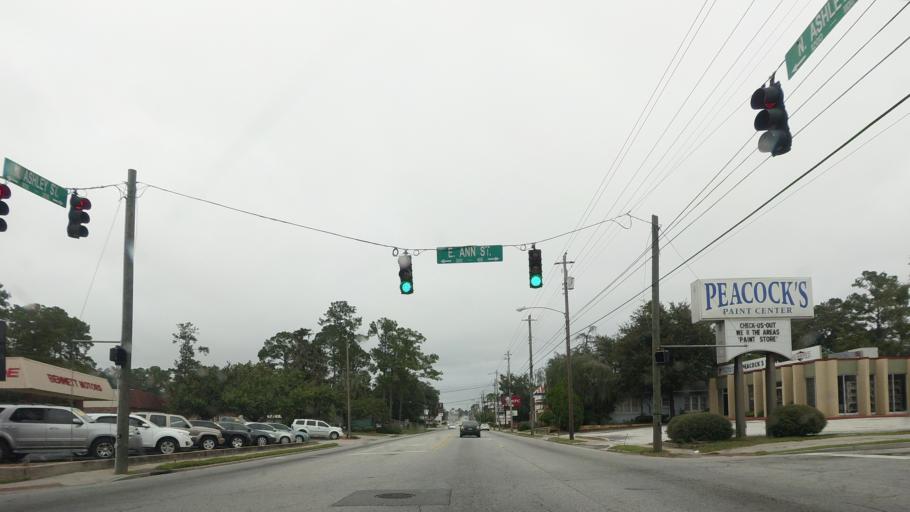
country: US
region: Georgia
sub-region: Lowndes County
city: Valdosta
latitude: 30.8451
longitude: -83.2803
